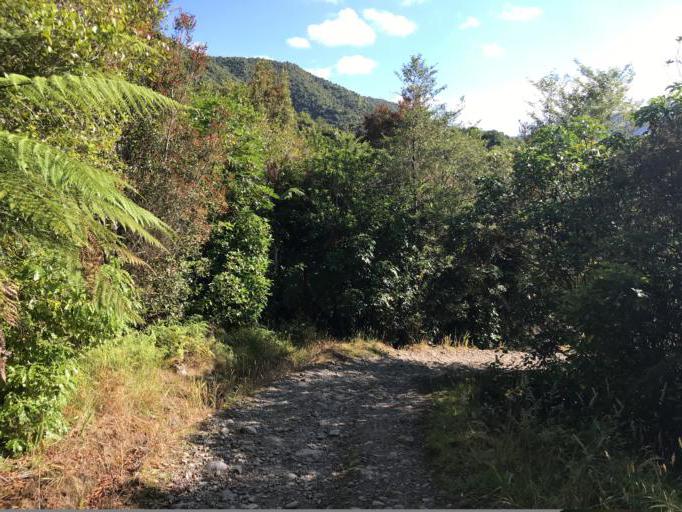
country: NZ
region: Wellington
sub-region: Kapiti Coast District
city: Otaki
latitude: -40.8723
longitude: 175.2319
